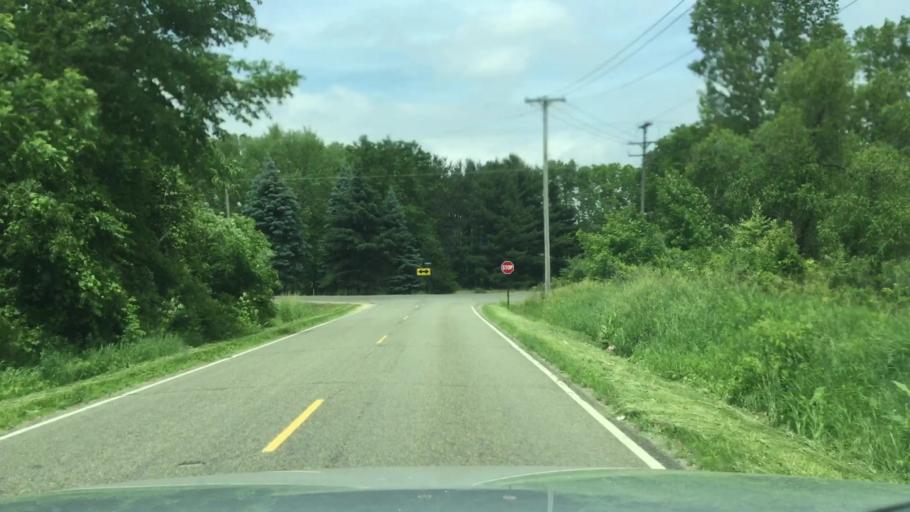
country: US
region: Michigan
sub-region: Shiawassee County
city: Durand
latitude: 42.9506
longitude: -83.9593
